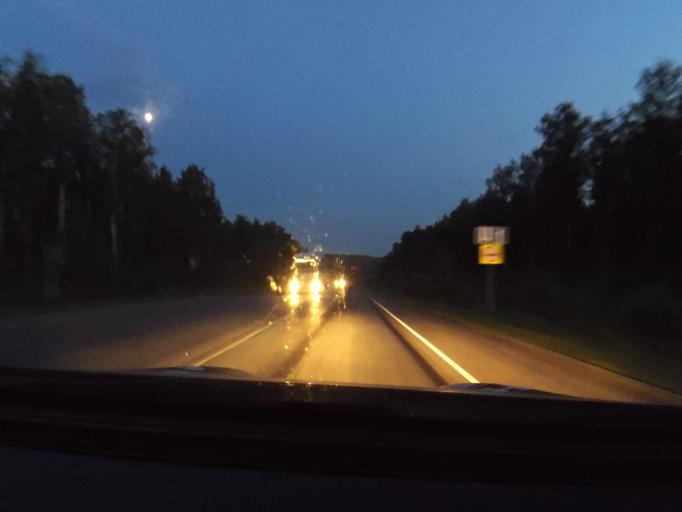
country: RU
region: Bashkortostan
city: Duvan
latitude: 55.9756
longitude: 58.2070
